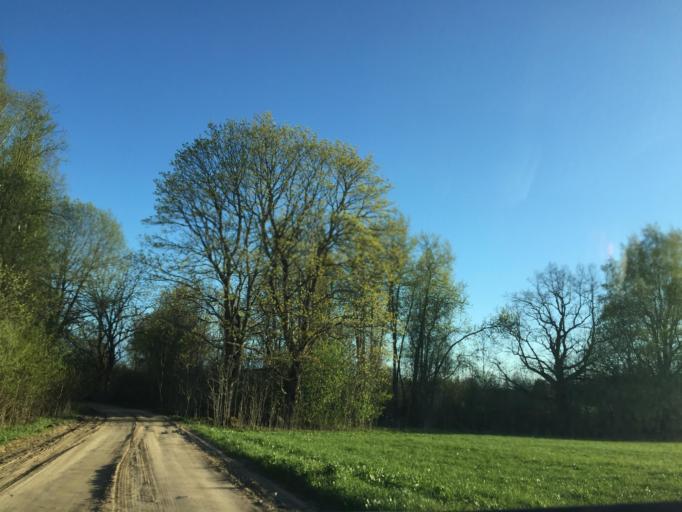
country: LV
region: Vecpiebalga
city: Vecpiebalga
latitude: 56.8459
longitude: 25.9573
